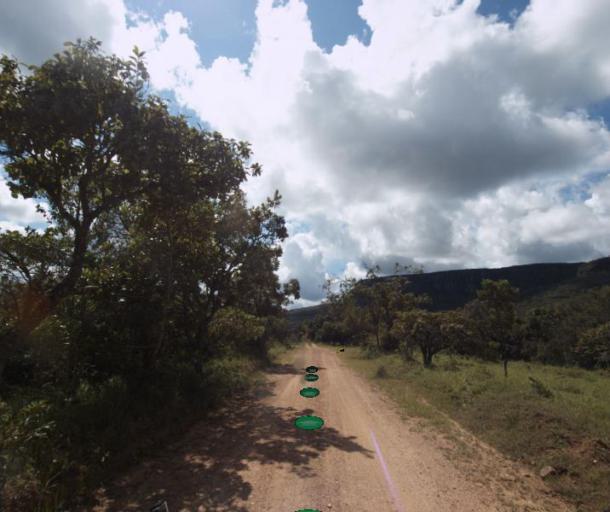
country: BR
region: Goias
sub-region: Pirenopolis
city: Pirenopolis
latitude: -15.7805
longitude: -48.9366
